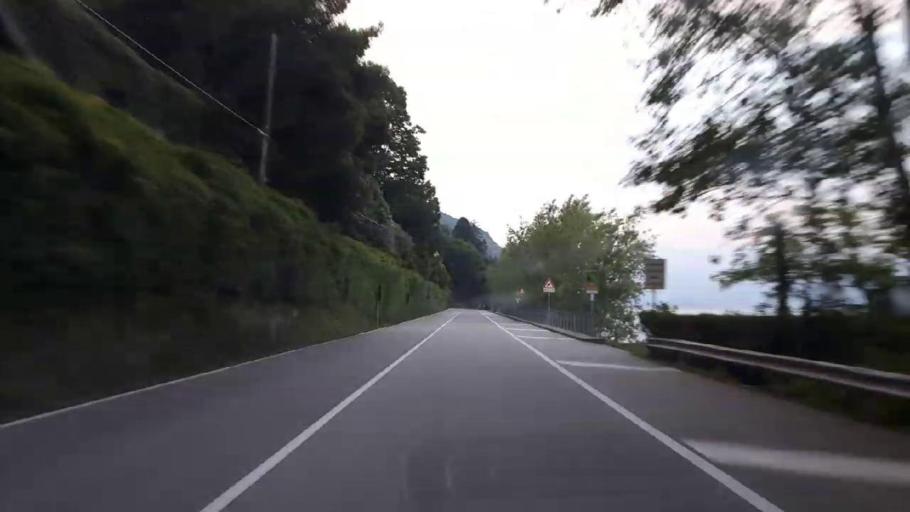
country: IT
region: Piedmont
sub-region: Provincia Verbano-Cusio-Ossola
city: Belgirate
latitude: 45.8457
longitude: 8.5722
